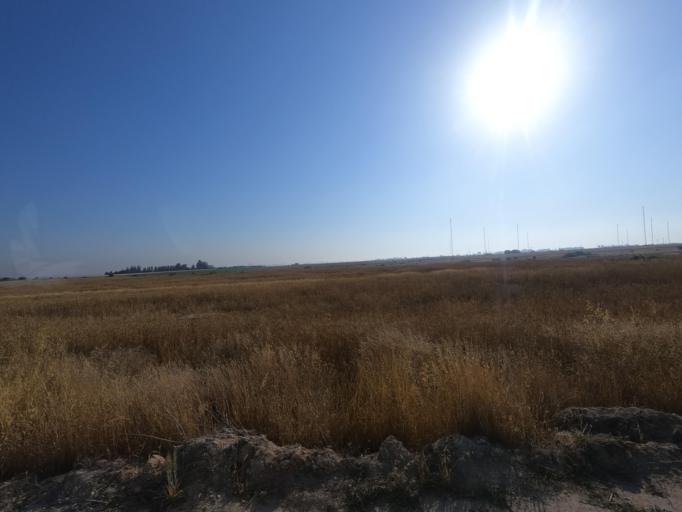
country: CY
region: Ammochostos
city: Acheritou
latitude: 35.0968
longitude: 33.8865
